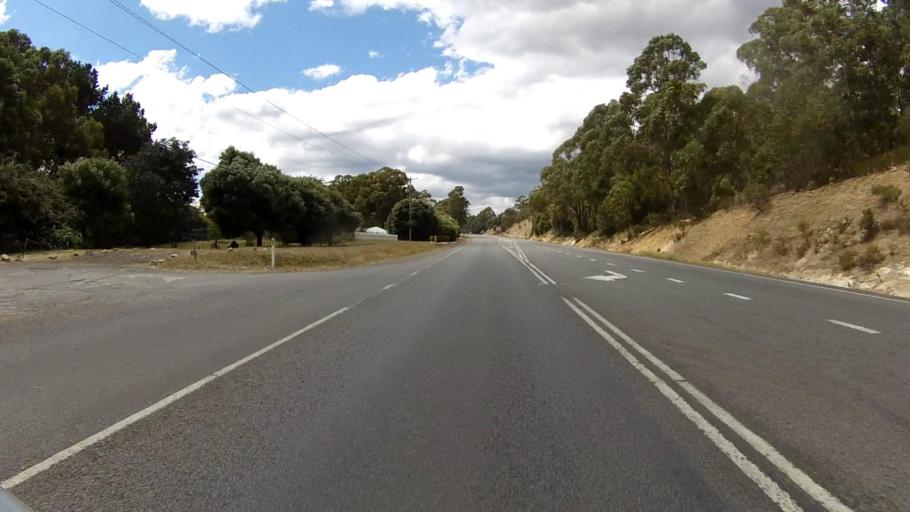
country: AU
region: Tasmania
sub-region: Huon Valley
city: Huonville
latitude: -42.9815
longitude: 147.0975
